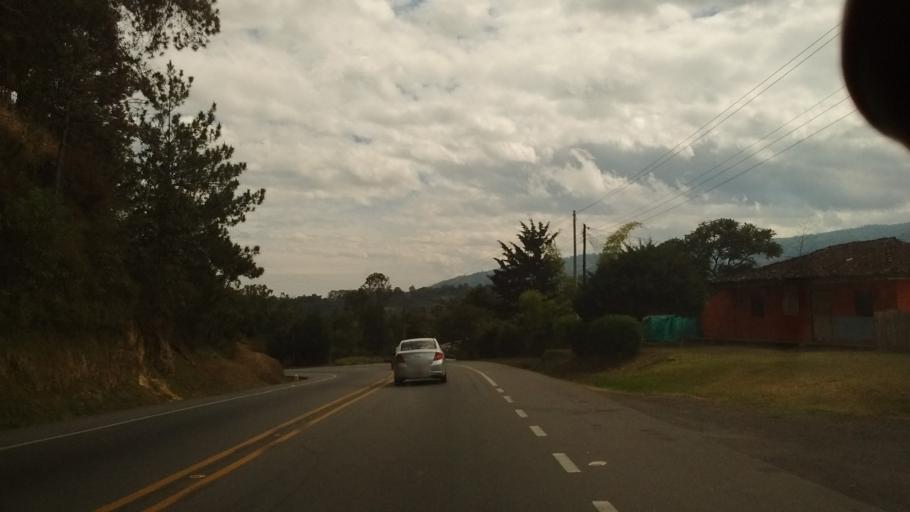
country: CO
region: Cauca
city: Cajibio
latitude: 2.5997
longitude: -76.5262
